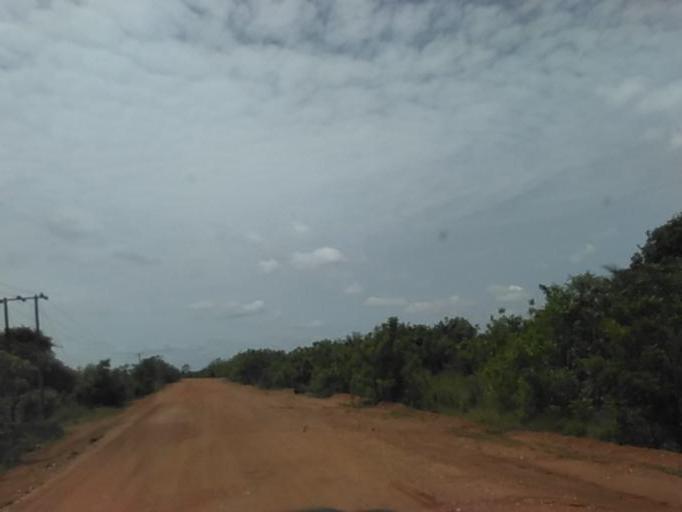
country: GH
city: Akropong
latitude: 6.0899
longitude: 0.2641
